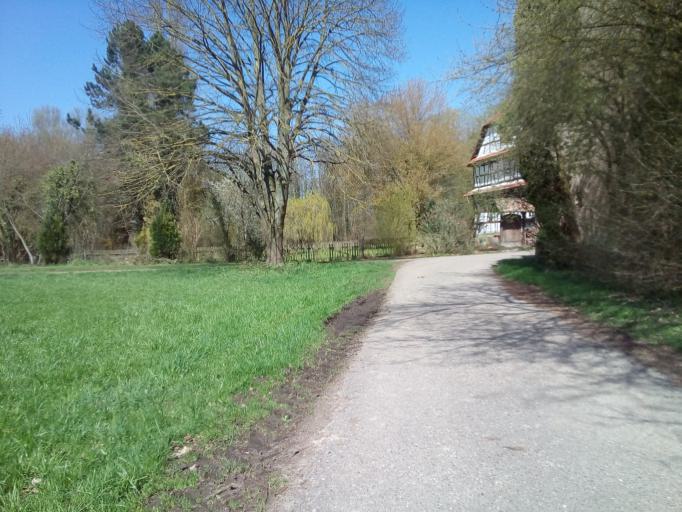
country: DE
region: Baden-Wuerttemberg
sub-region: Freiburg Region
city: Rheinau
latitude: 48.6558
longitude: 7.9119
